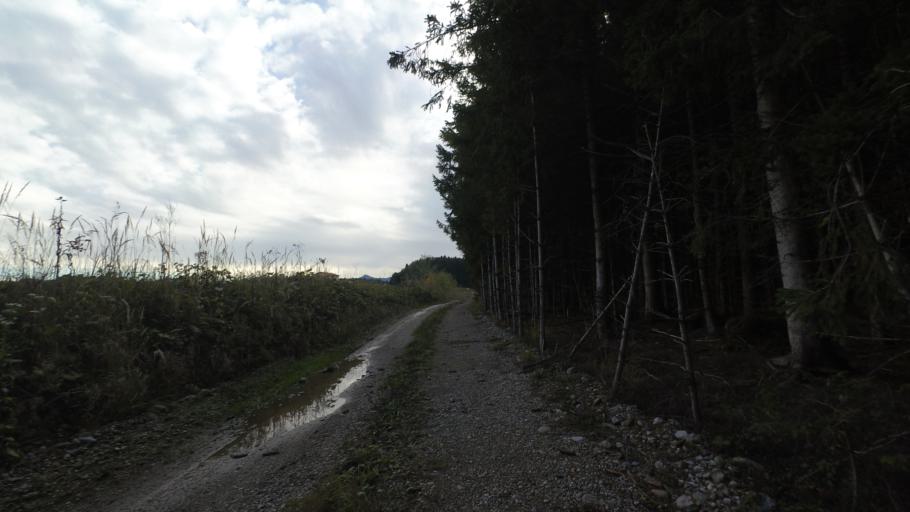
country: DE
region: Bavaria
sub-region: Upper Bavaria
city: Nussdorf
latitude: 47.9297
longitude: 12.5874
